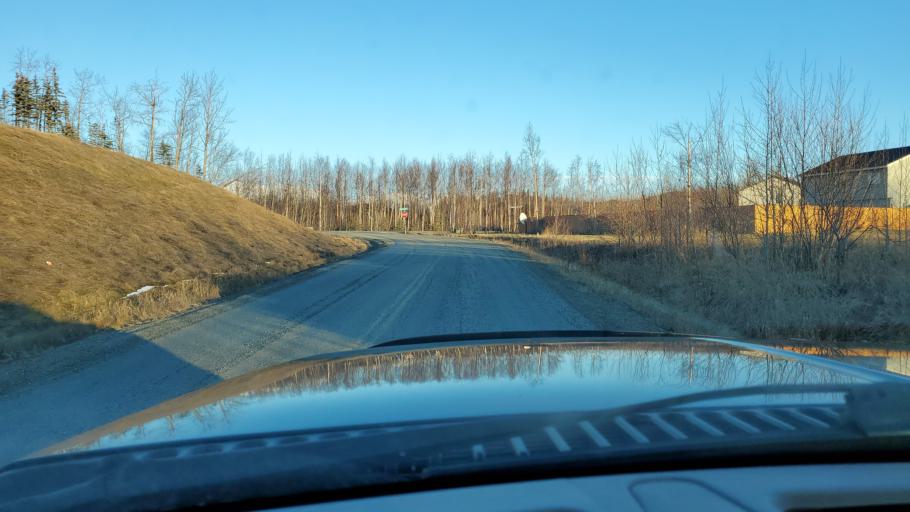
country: US
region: Alaska
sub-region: Matanuska-Susitna Borough
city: Gateway
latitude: 61.5877
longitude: -149.2587
